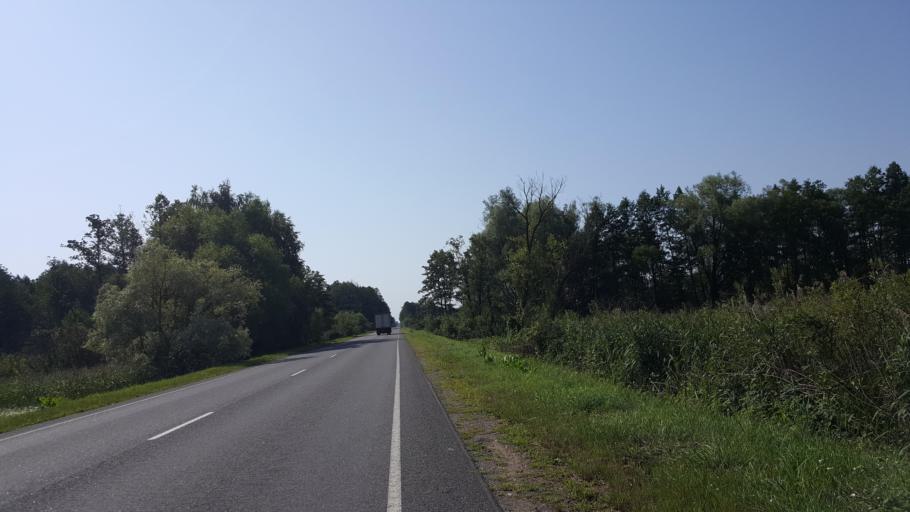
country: BY
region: Brest
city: Zhabinka
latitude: 52.2761
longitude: 23.9516
